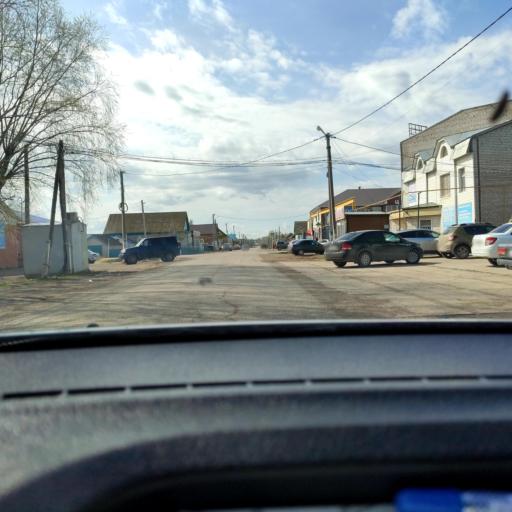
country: RU
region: Bashkortostan
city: Starobaltachevo
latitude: 56.0020
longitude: 55.9313
